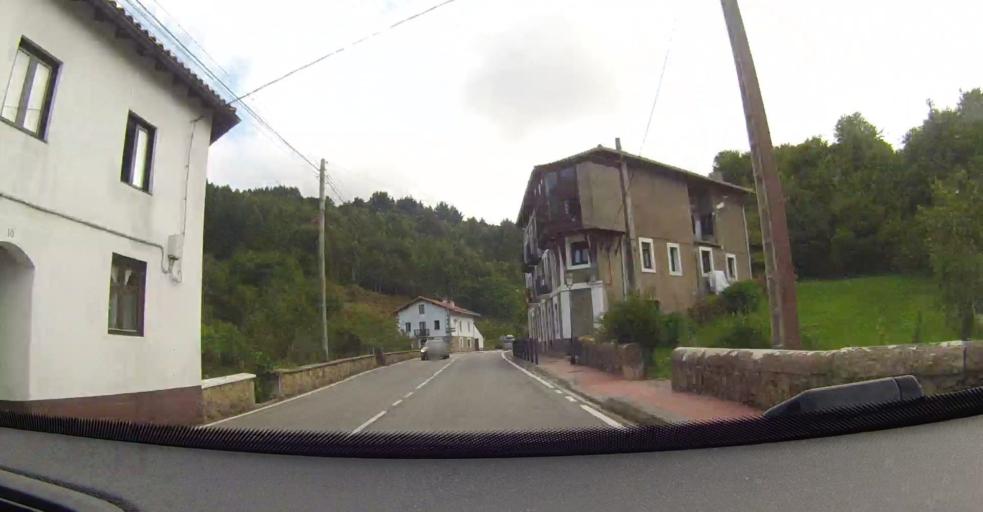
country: ES
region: Basque Country
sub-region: Bizkaia
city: Ibarrangelu
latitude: 43.3882
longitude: -2.6316
